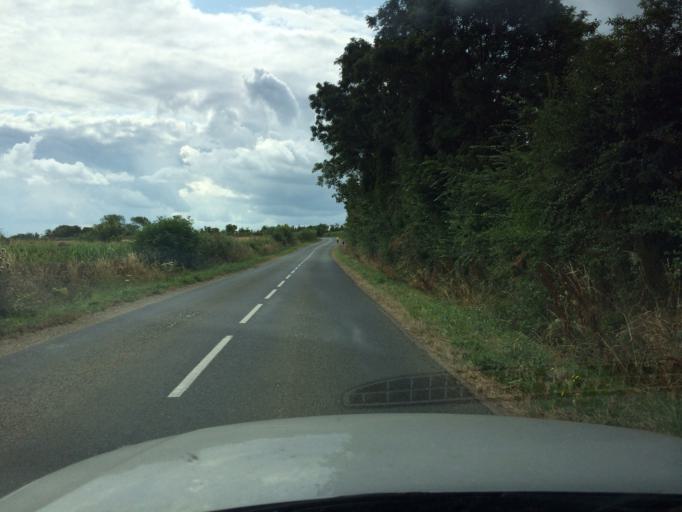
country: FR
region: Lower Normandy
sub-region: Departement de la Manche
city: Sainte-Mere-Eglise
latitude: 49.4519
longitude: -1.2655
